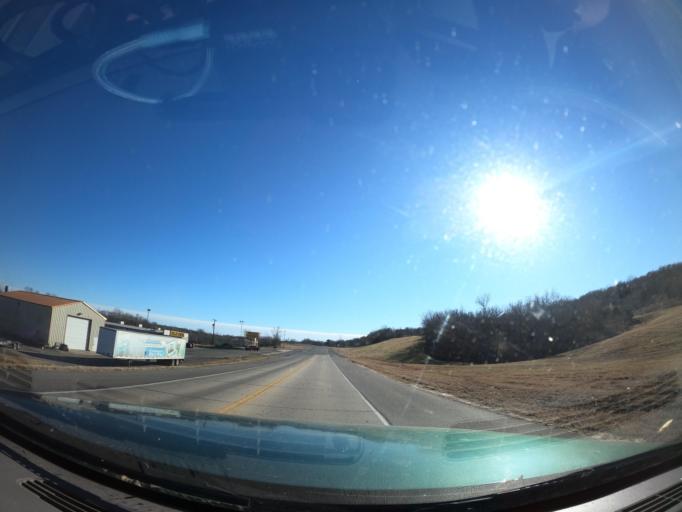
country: US
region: Oklahoma
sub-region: McIntosh County
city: Eufaula
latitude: 35.2726
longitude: -95.5856
